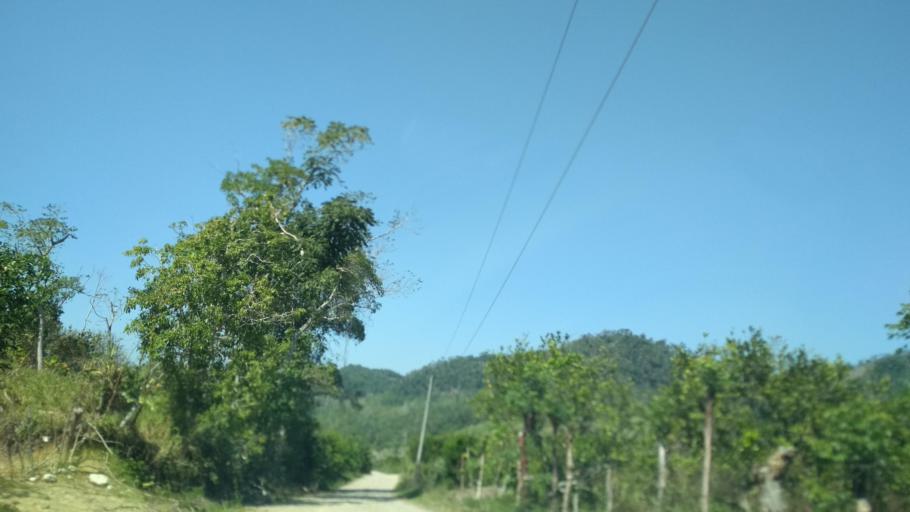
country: MX
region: Veracruz
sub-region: Papantla
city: Polutla
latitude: 20.4770
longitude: -97.2199
